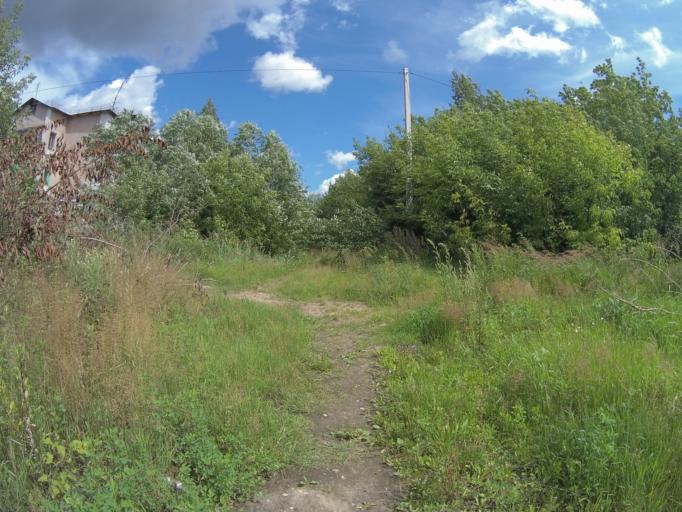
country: RU
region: Vladimir
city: Vladimir
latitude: 56.1357
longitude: 40.4139
